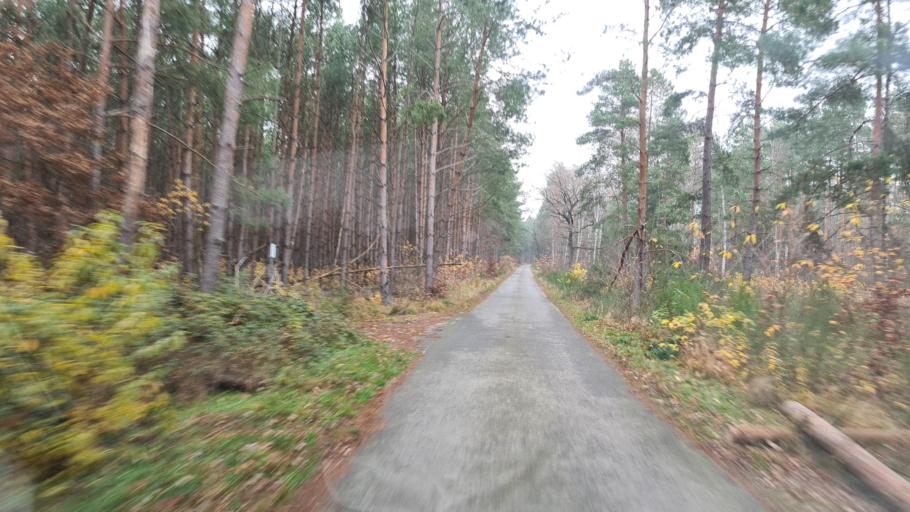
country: DE
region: Brandenburg
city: Groden
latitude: 51.3804
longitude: 13.5517
